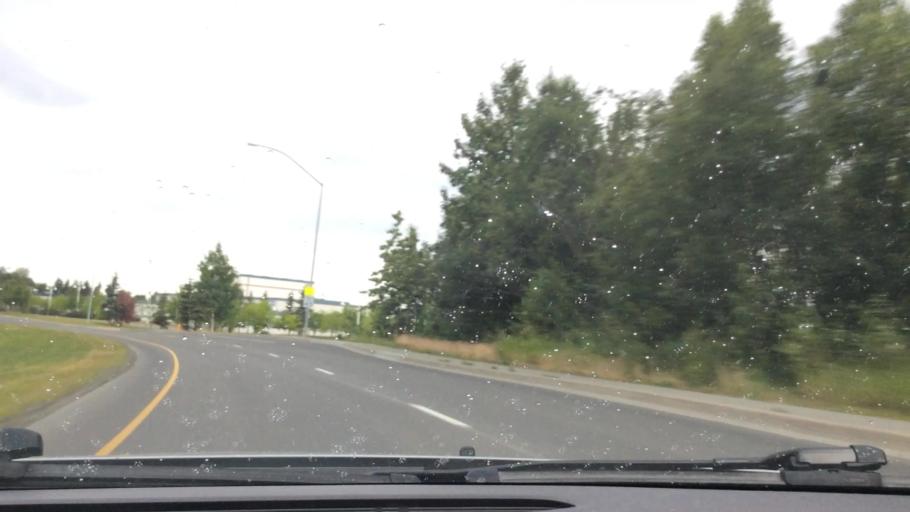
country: US
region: Alaska
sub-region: Anchorage Municipality
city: Anchorage
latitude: 61.1988
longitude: -149.7997
